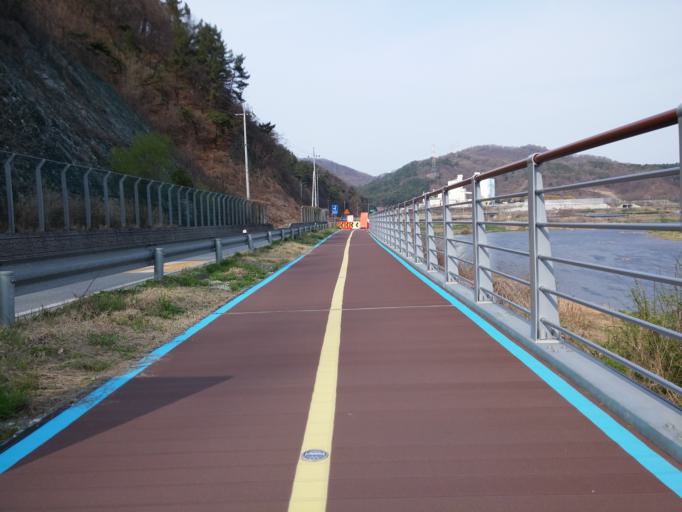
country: KR
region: Daejeon
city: Songgang-dong
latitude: 36.4983
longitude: 127.3777
